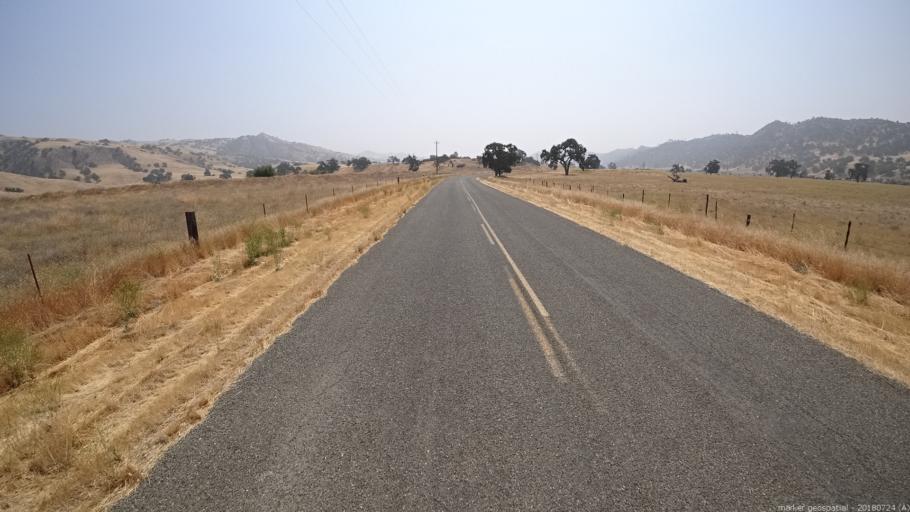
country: US
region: California
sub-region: Monterey County
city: King City
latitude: 36.1820
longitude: -120.7992
